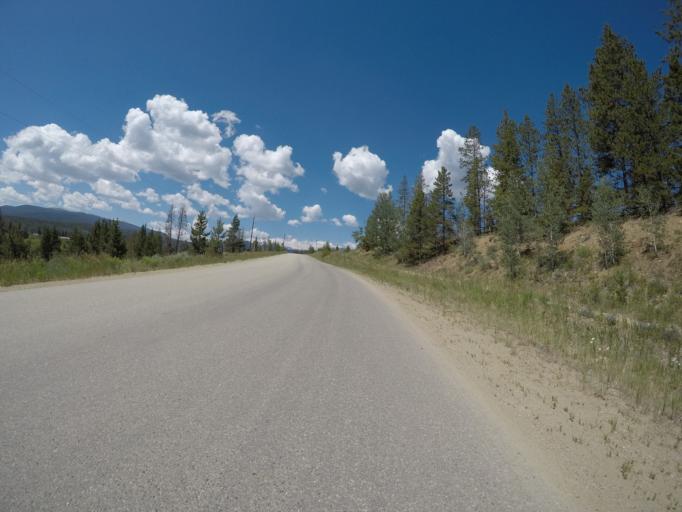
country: US
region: Colorado
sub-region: Grand County
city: Fraser
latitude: 39.9446
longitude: -105.8308
